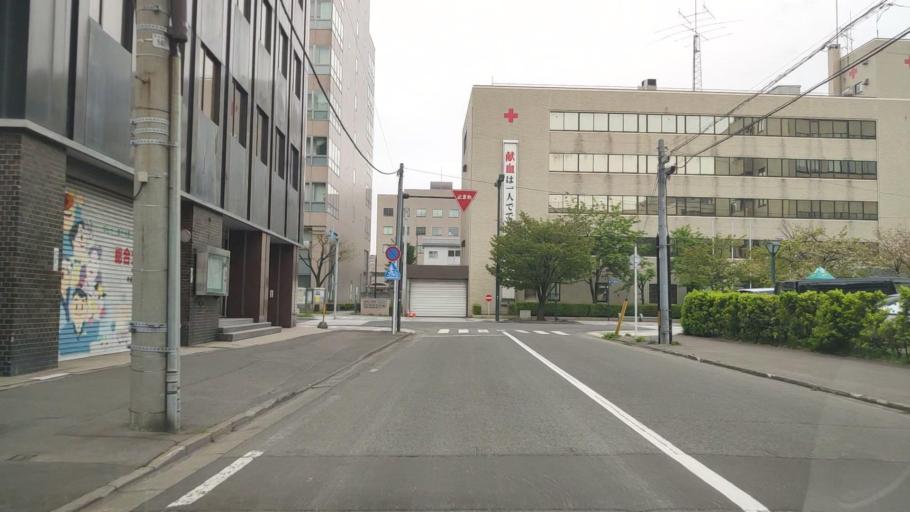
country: JP
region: Aomori
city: Aomori Shi
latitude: 40.8250
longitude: 140.7436
